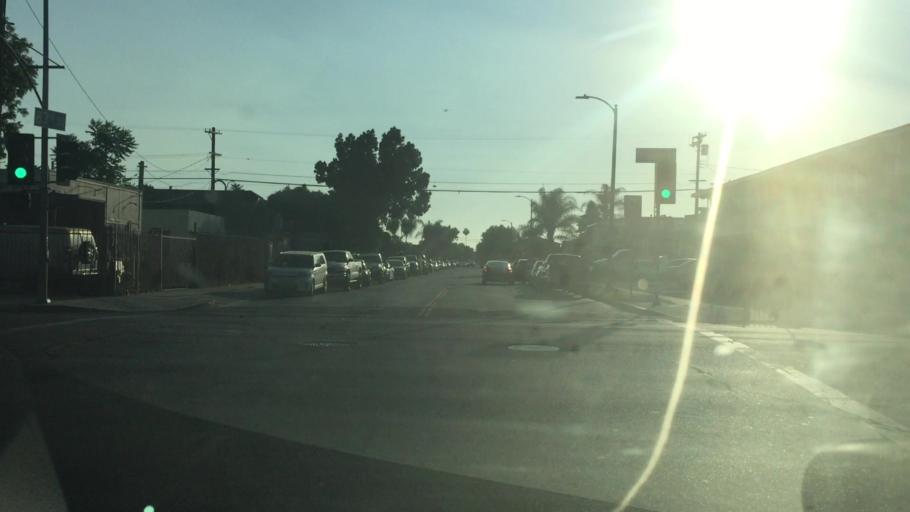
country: US
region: California
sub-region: Los Angeles County
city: Florence-Graham
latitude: 33.9638
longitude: -118.2651
